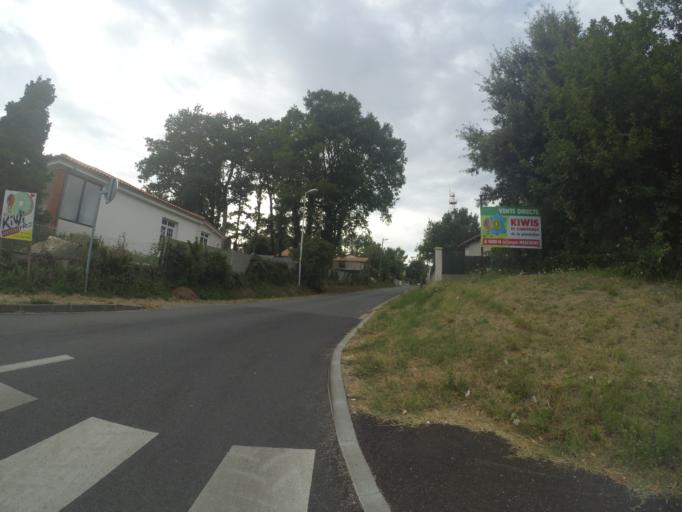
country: FR
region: Poitou-Charentes
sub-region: Departement de la Charente-Maritime
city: Meschers-sur-Gironde
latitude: 45.5658
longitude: -0.9615
